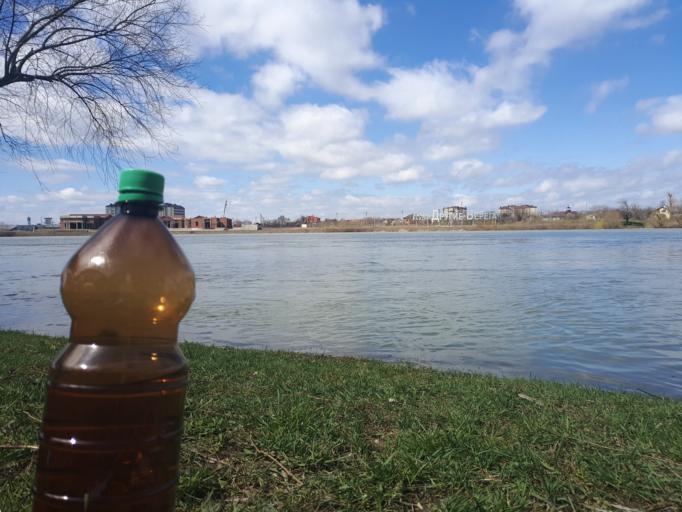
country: RU
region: Krasnodarskiy
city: Krasnodar
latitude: 45.0227
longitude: 38.9519
